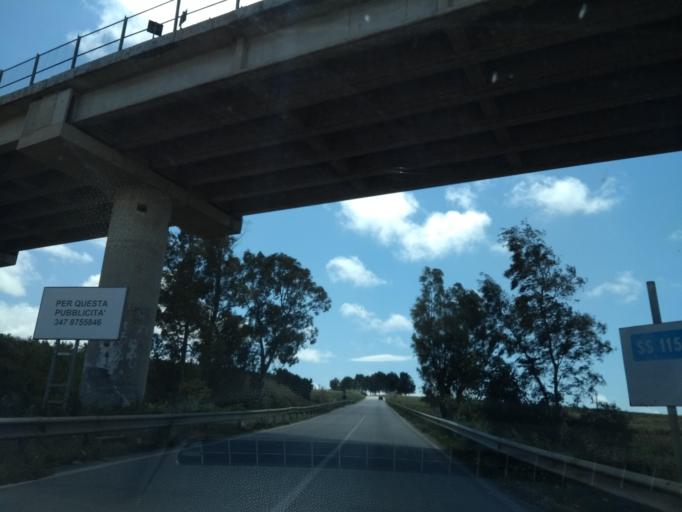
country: IT
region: Sicily
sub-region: Trapani
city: Marsala
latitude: 37.8809
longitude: 12.5241
